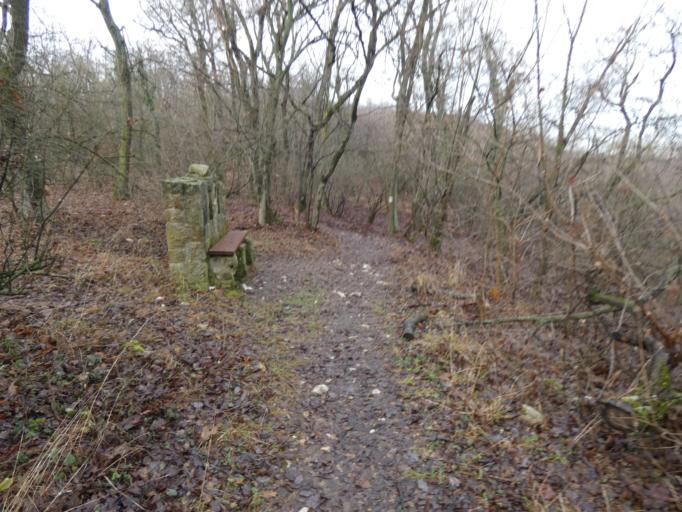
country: HU
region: Pest
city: Csobanka
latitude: 47.6271
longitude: 18.9768
